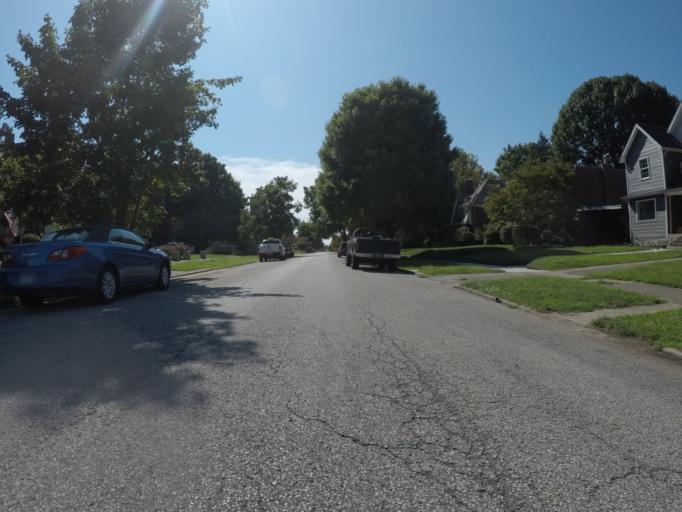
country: US
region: Ohio
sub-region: Lawrence County
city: Ironton
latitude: 38.5316
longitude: -82.6794
